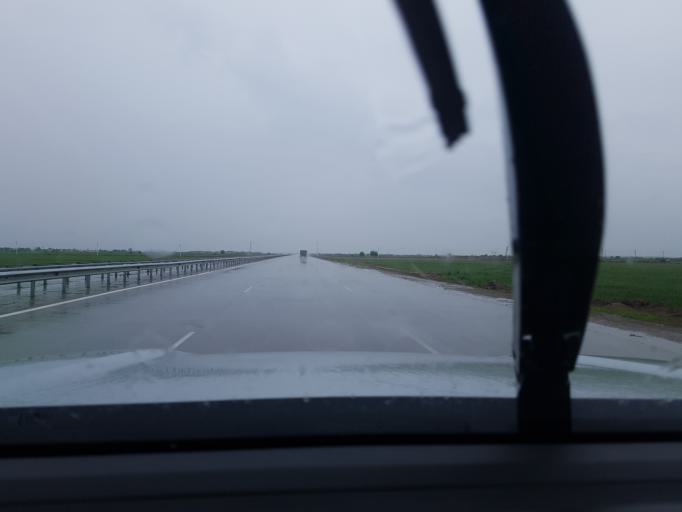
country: TM
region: Lebap
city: Farap
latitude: 39.1769
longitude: 63.5668
